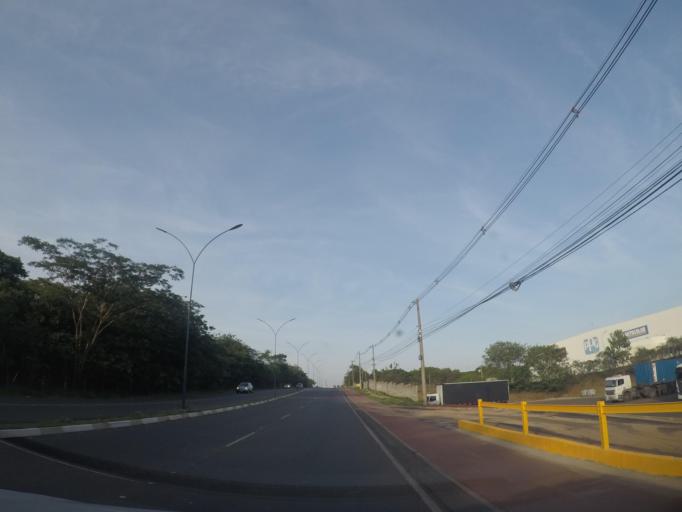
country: BR
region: Sao Paulo
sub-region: Hortolandia
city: Hortolandia
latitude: -22.8472
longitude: -47.1734
